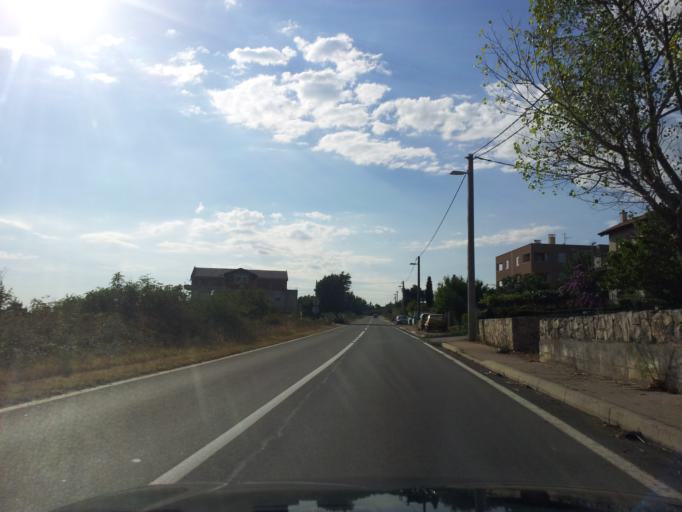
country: HR
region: Zadarska
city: Posedarje
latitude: 44.2168
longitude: 15.4661
